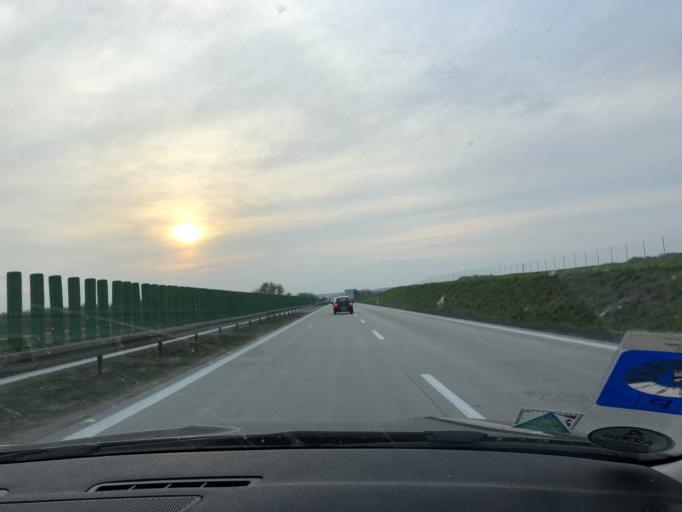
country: PL
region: Lower Silesian Voivodeship
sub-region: Powiat legnicki
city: Chojnow
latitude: 51.2372
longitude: 15.9036
